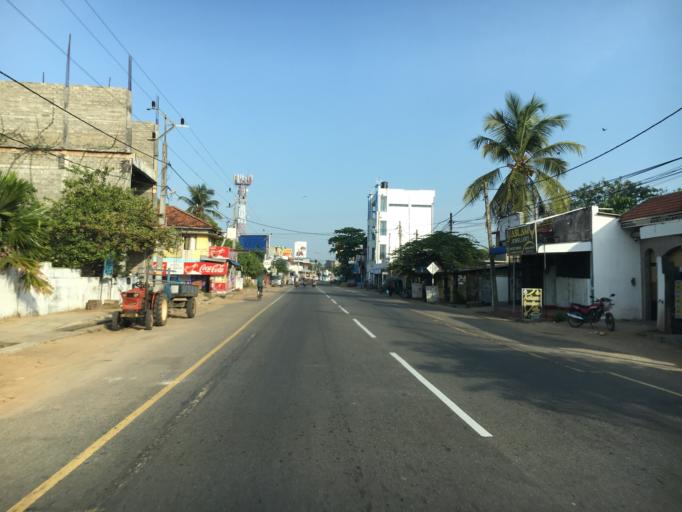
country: LK
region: Eastern Province
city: Eravur Town
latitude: 7.9137
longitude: 81.5243
